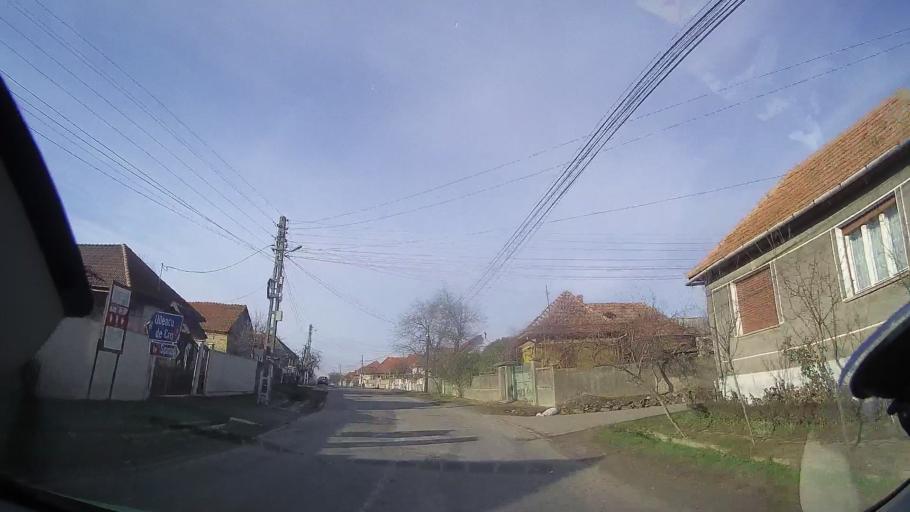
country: RO
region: Bihor
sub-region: Comuna Brusturi
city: Brusturi
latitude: 47.1484
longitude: 22.2542
